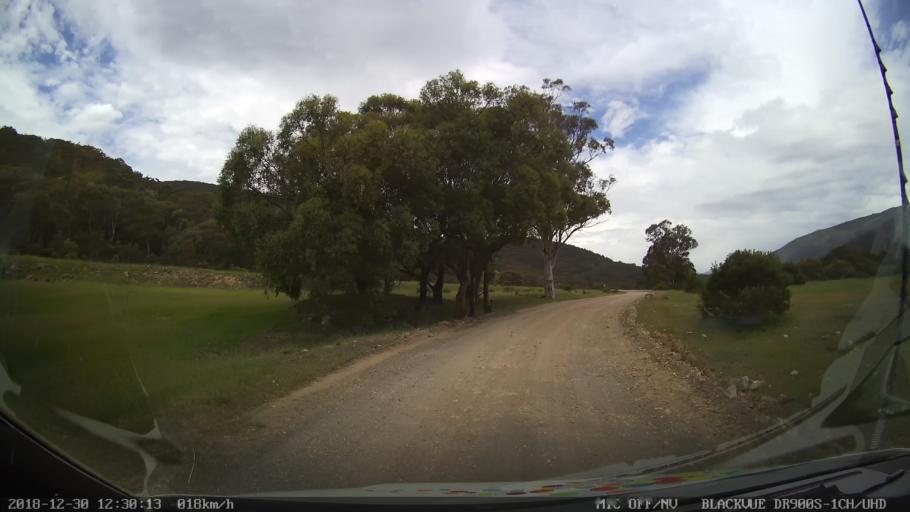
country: AU
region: New South Wales
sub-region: Snowy River
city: Jindabyne
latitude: -36.3238
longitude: 148.4751
